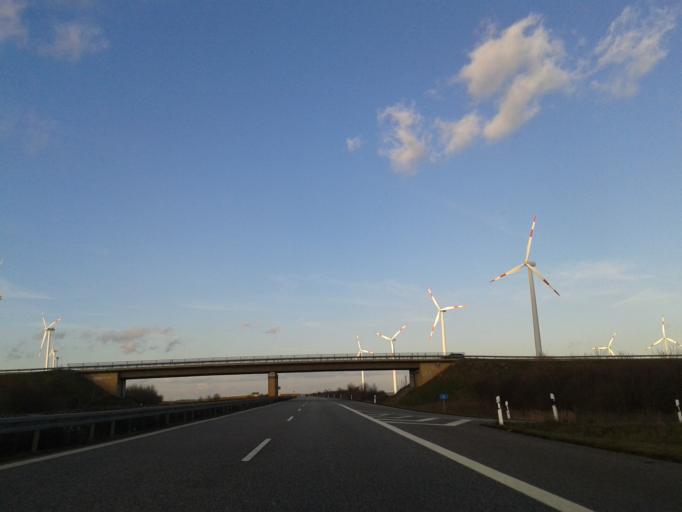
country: DE
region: Saxony-Anhalt
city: Holleben
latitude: 51.4252
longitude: 11.8641
